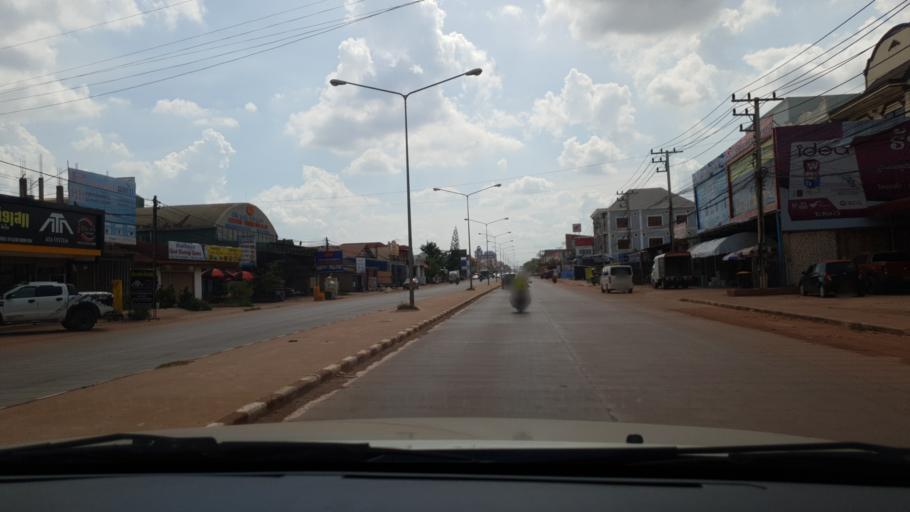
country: LA
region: Vientiane
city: Vientiane
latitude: 18.0313
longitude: 102.6500
